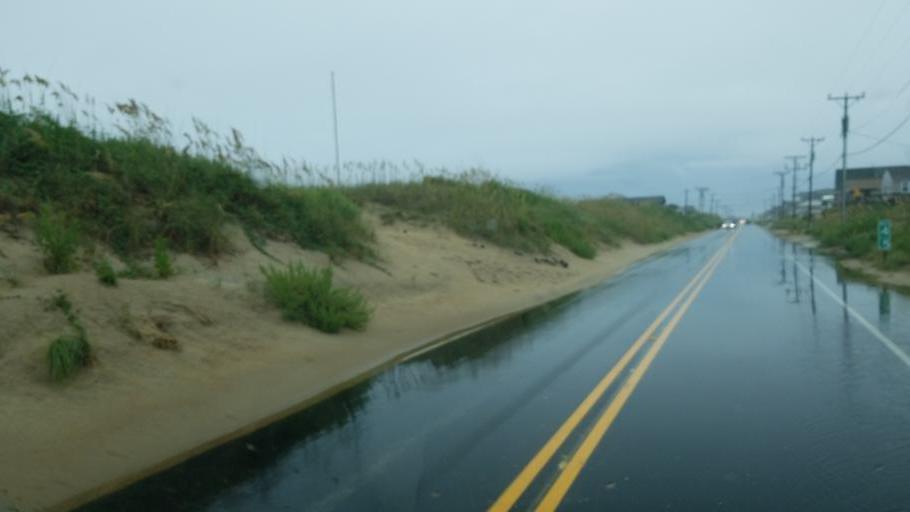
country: US
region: North Carolina
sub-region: Dare County
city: Kitty Hawk
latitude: 36.0639
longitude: -75.6885
